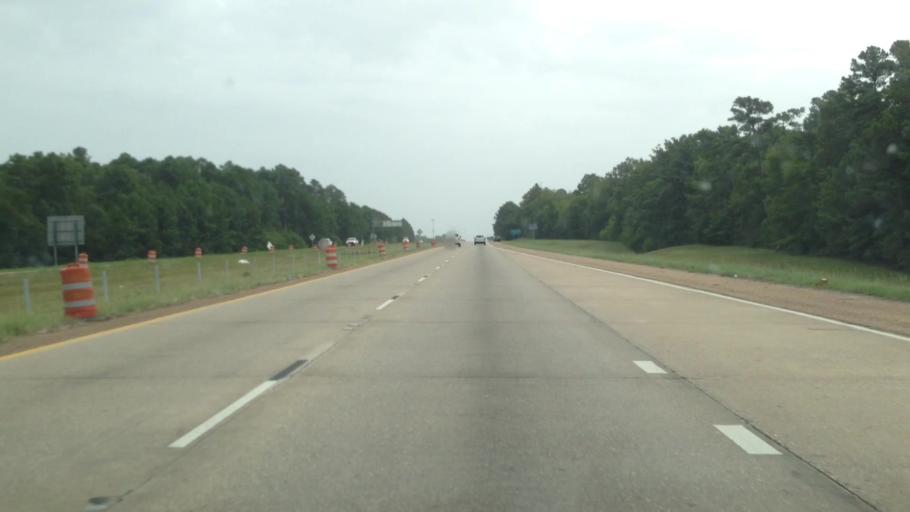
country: US
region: Louisiana
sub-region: Caddo Parish
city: Shreveport
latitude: 32.4775
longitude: -93.8340
